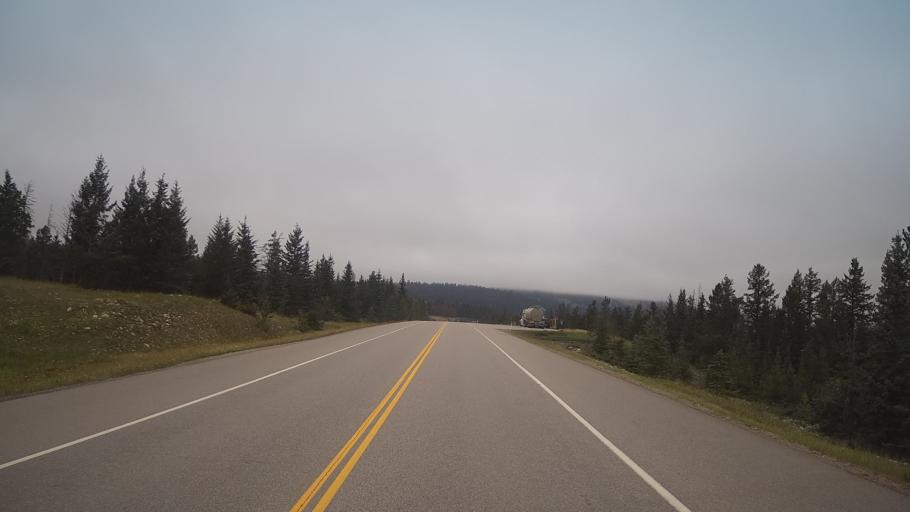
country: CA
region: Alberta
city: Jasper Park Lodge
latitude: 52.8751
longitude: -118.0716
